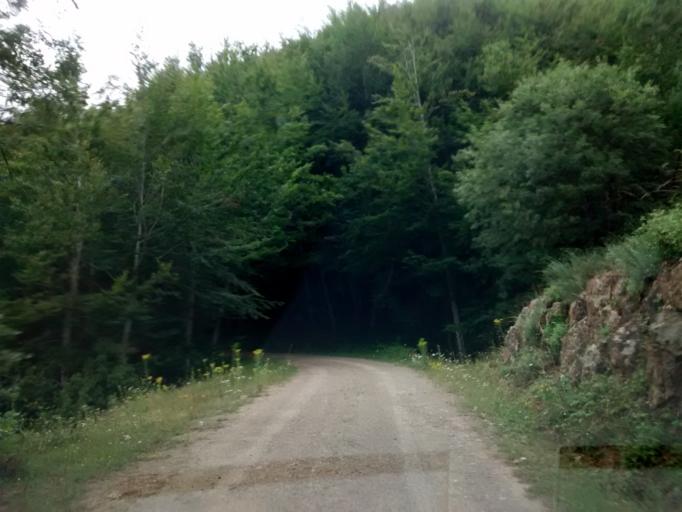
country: ES
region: La Rioja
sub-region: Provincia de La Rioja
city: Ajamil
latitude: 42.1396
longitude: -2.4814
